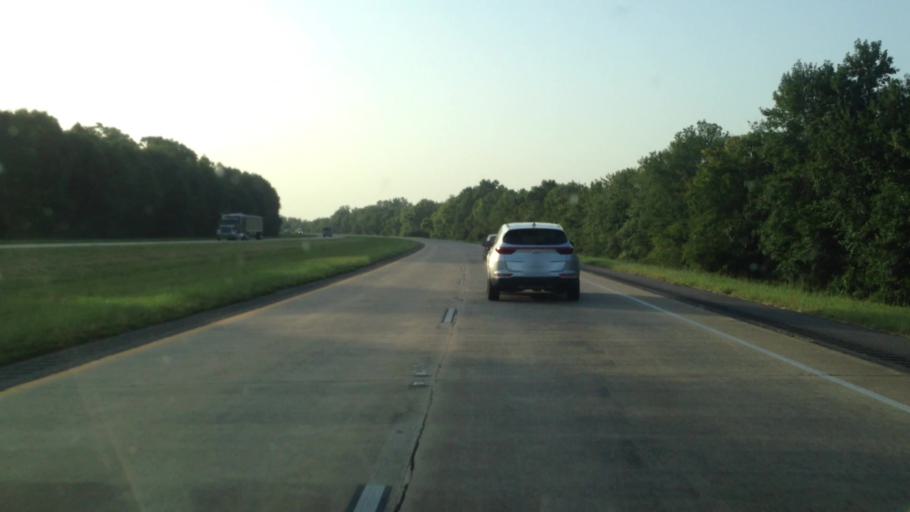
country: US
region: Louisiana
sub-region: Natchitoches Parish
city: Vienna Bend
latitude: 31.5719
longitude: -93.0146
